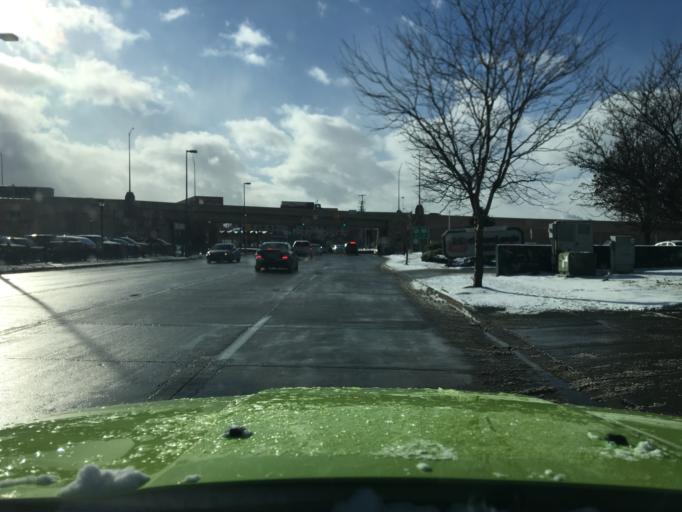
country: US
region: Michigan
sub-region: Kent County
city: Grand Rapids
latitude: 42.9619
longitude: -85.6745
